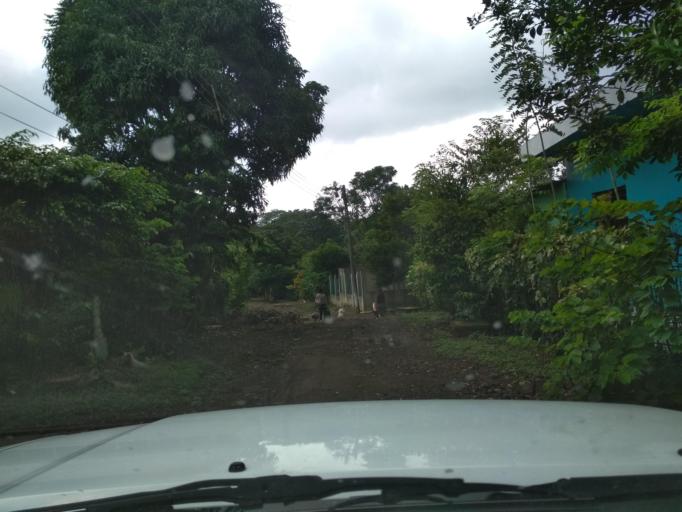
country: MX
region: Veracruz
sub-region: San Andres Tuxtla
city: El Huidero
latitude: 18.3872
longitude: -95.1790
